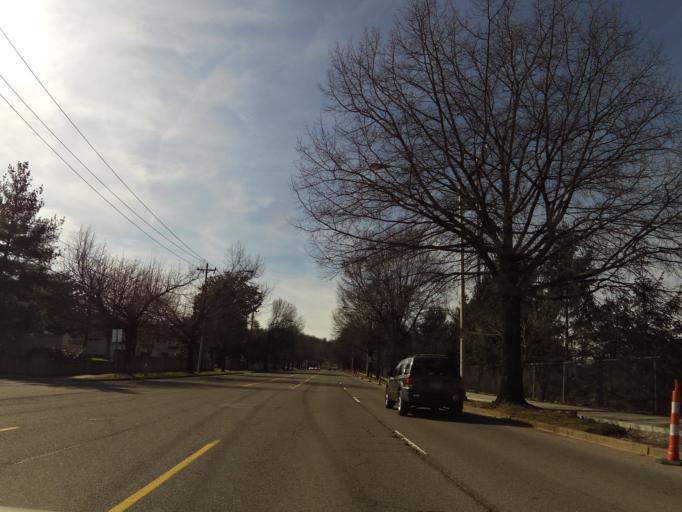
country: US
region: Tennessee
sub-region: Davidson County
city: Nashville
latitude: 36.1383
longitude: -86.8077
